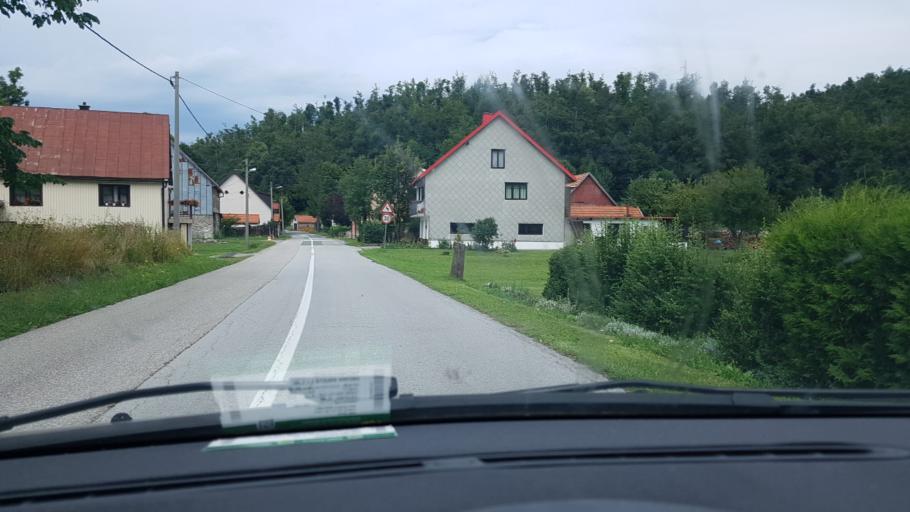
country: HR
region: Primorsko-Goranska
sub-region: Grad Delnice
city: Delnice
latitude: 45.3285
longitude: 14.7414
